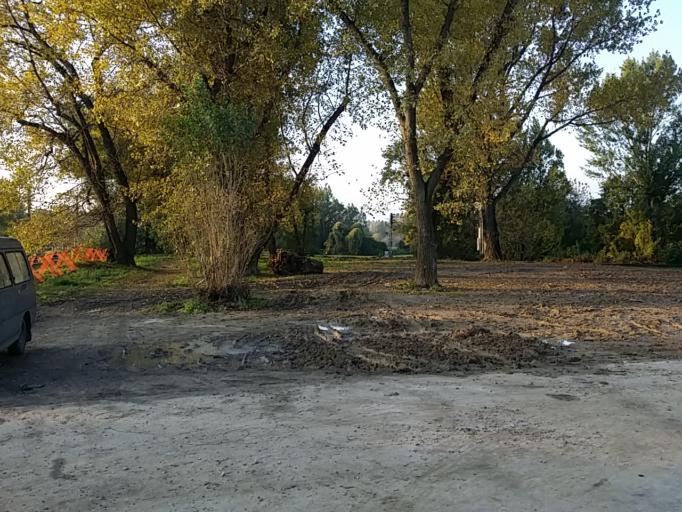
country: HU
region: Budapest
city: Budapest III. keruelet
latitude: 47.5659
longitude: 19.0485
